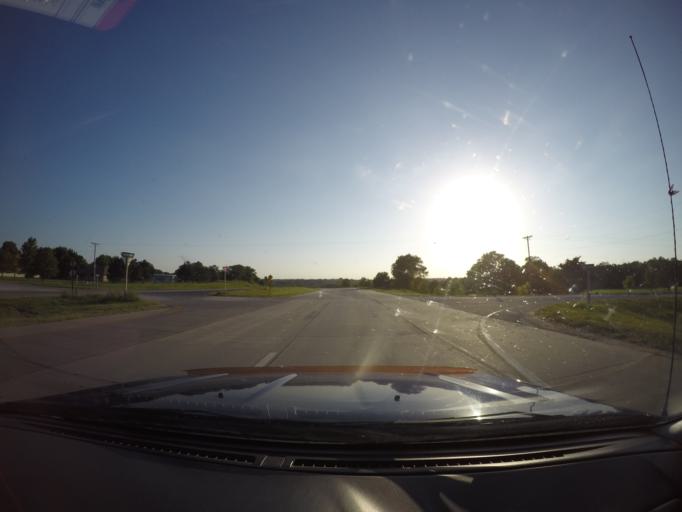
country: US
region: Kansas
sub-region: Pottawatomie County
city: Wamego
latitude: 39.2094
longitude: -96.4122
